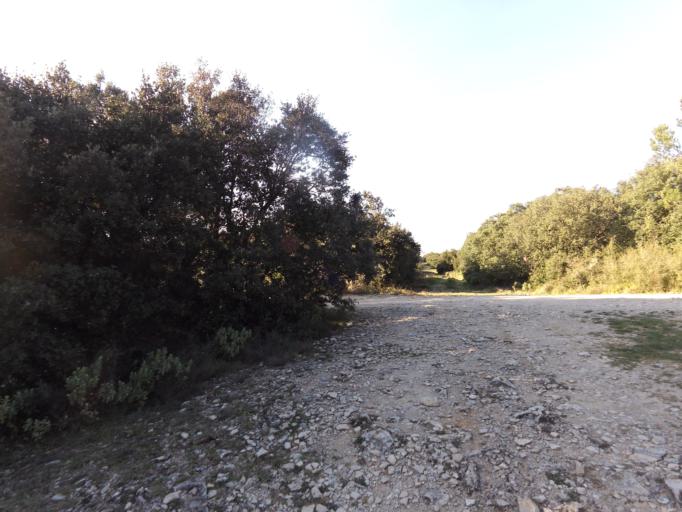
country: FR
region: Languedoc-Roussillon
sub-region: Departement du Gard
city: Clarensac
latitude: 43.8360
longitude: 4.1935
